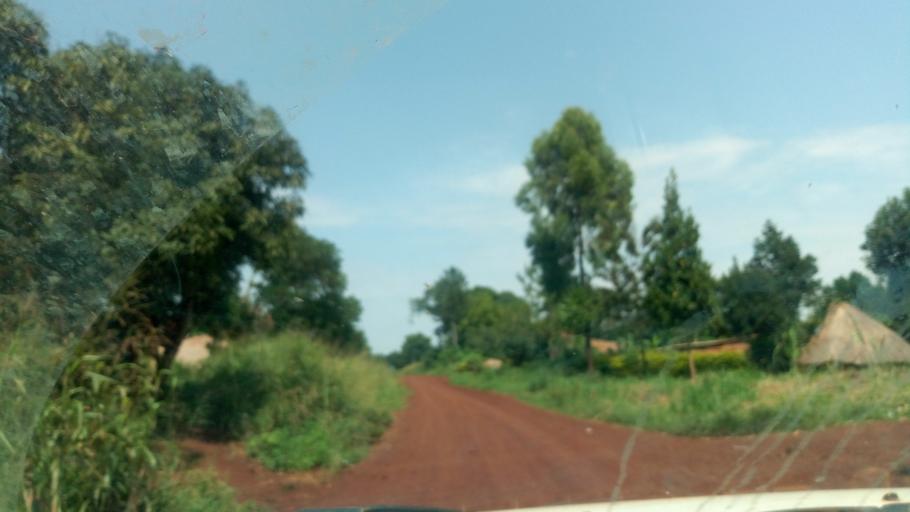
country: UG
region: Western Region
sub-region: Masindi District
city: Masindi
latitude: 1.6700
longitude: 31.8237
